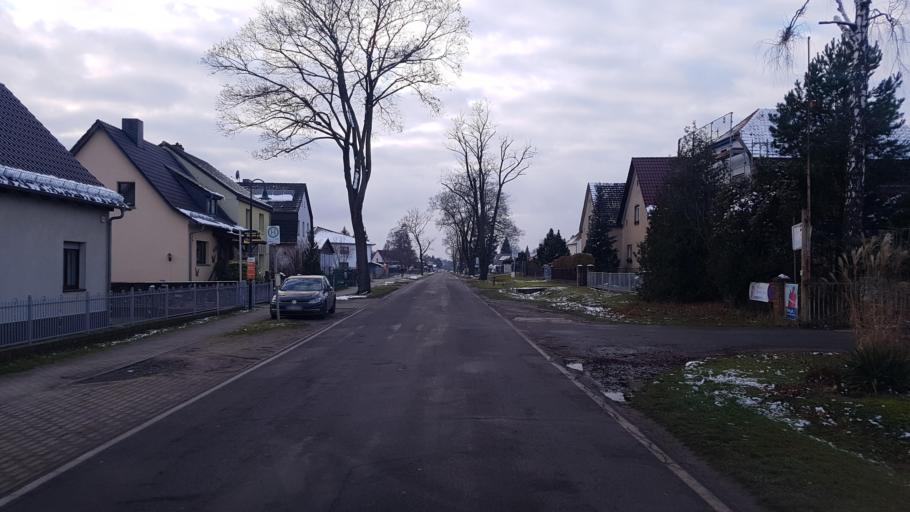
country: DE
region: Brandenburg
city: Rehfelde
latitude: 52.5089
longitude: 13.8619
